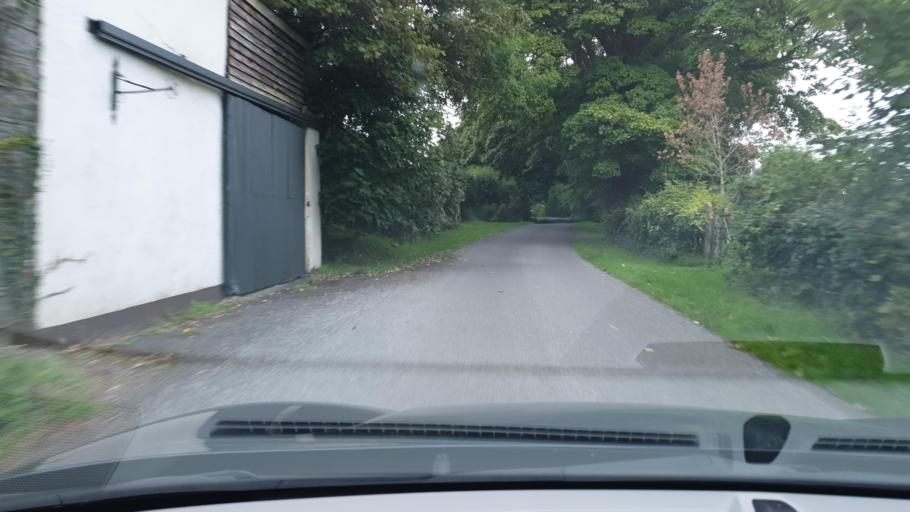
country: IE
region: Leinster
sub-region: An Mhi
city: Dunshaughlin
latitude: 53.4938
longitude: -6.5503
